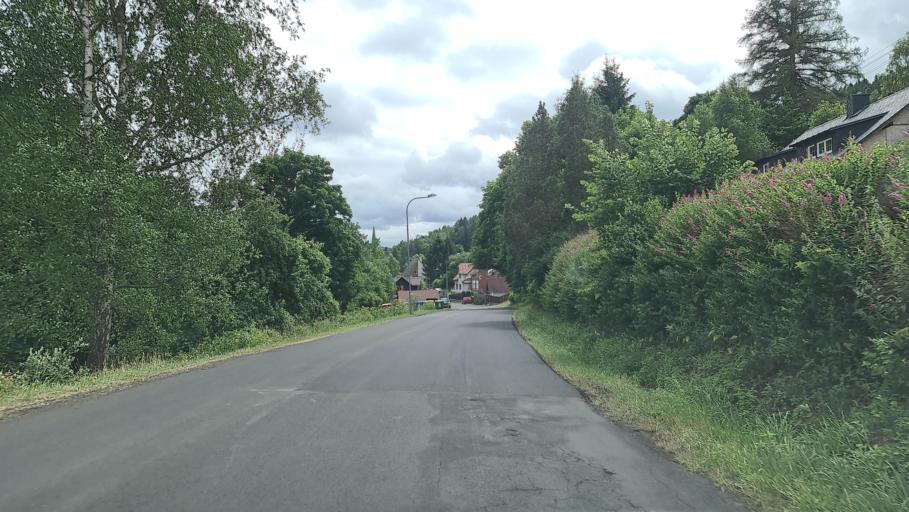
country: CZ
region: Karlovarsky
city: Kraslice
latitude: 50.3638
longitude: 12.5233
